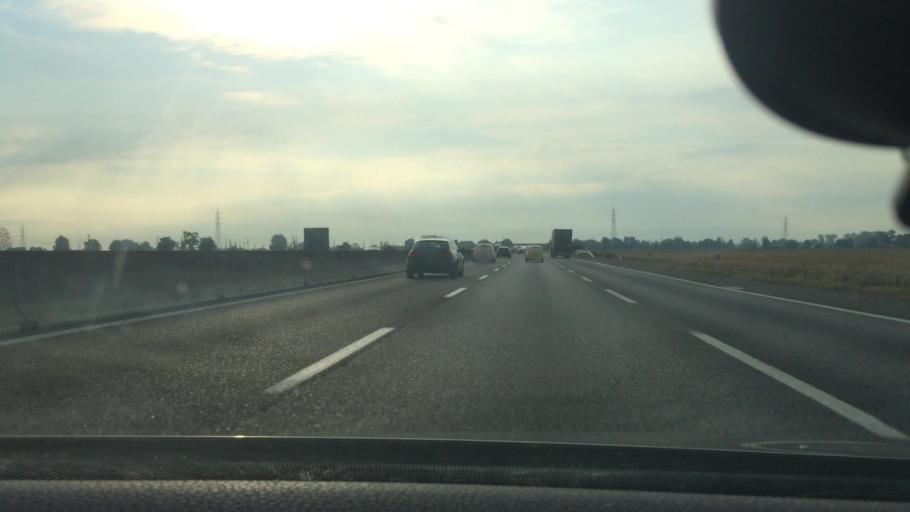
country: IT
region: Lombardy
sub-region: Provincia di Lodi
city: Salerano sul Lambro
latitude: 45.3132
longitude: 9.3875
